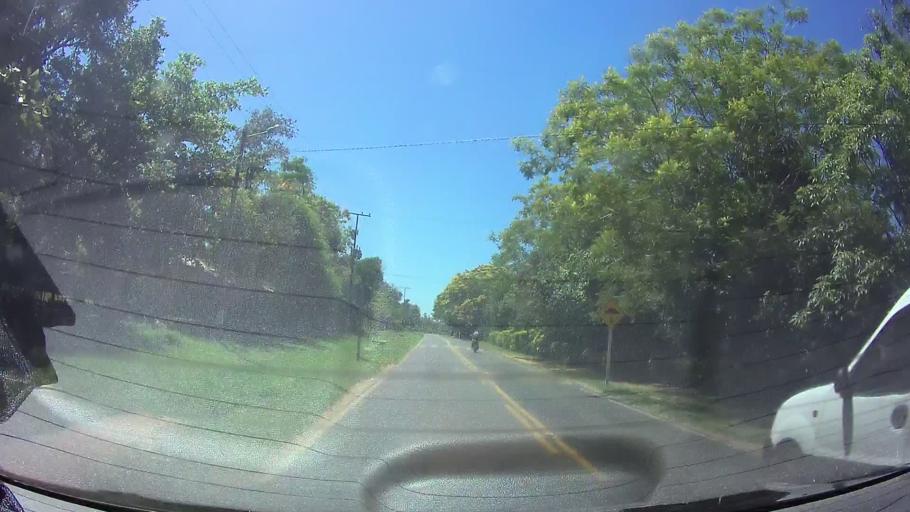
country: PY
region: Central
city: Aregua
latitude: -25.2777
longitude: -57.4047
